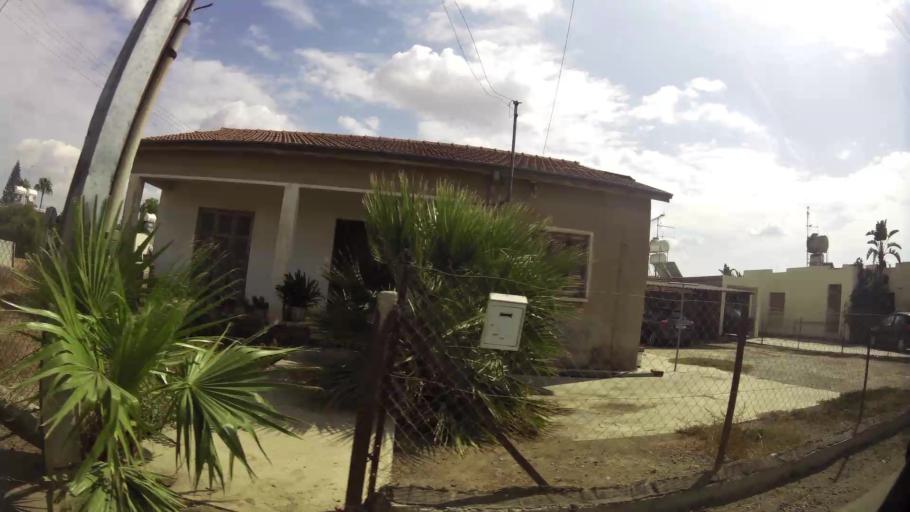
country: CY
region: Lefkosia
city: Tseri
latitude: 35.0706
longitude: 33.3247
